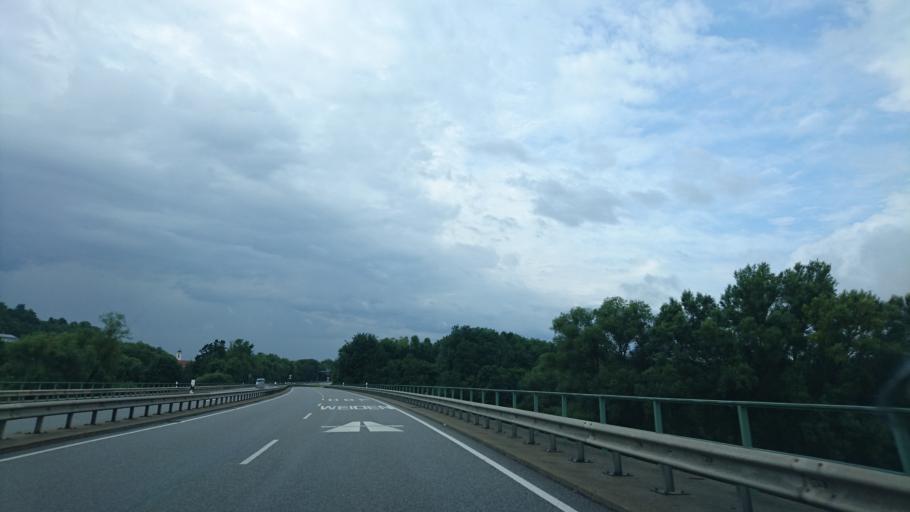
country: DE
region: Bavaria
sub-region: Upper Palatinate
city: Lappersdorf
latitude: 49.0468
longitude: 12.0980
